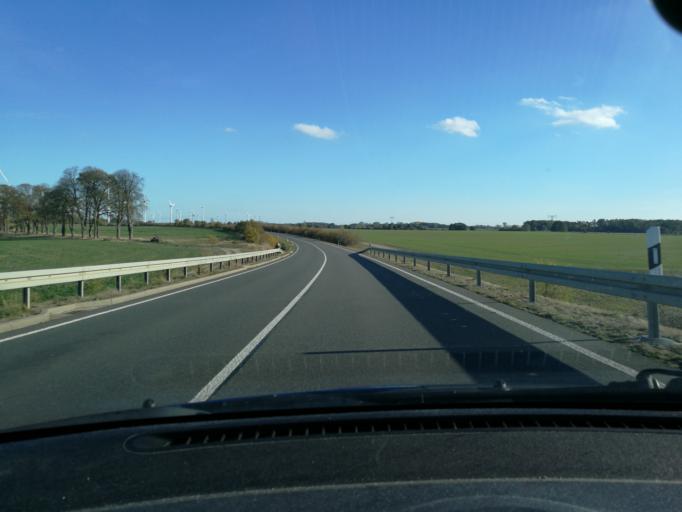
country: DE
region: Brandenburg
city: Karstadt
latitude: 53.1460
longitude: 11.7440
